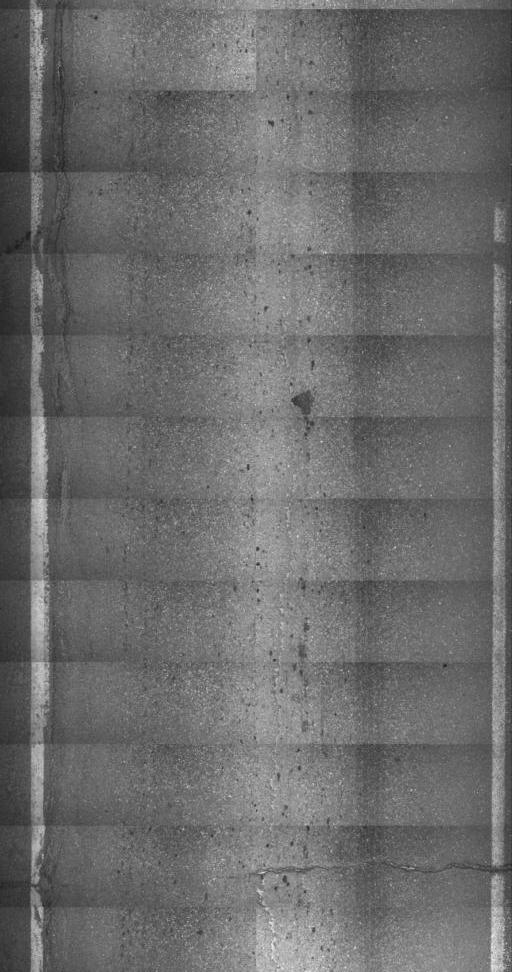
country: US
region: Vermont
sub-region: Orleans County
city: Newport
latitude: 44.9505
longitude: -72.1642
